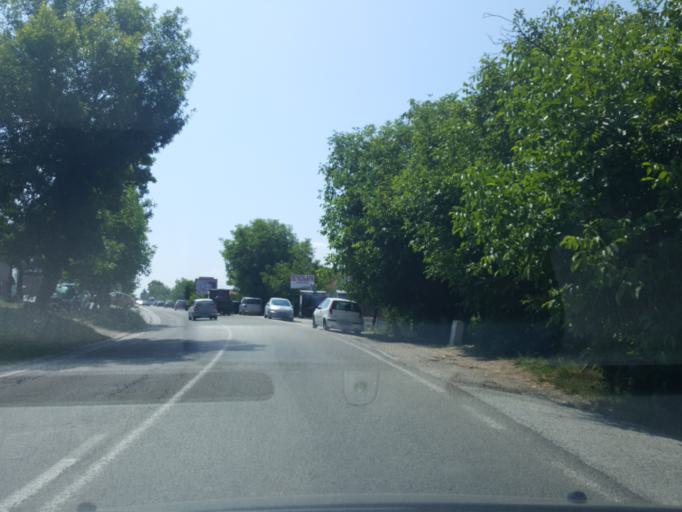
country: RS
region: Central Serbia
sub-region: Belgrade
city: Mladenovac
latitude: 44.4561
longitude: 20.6768
